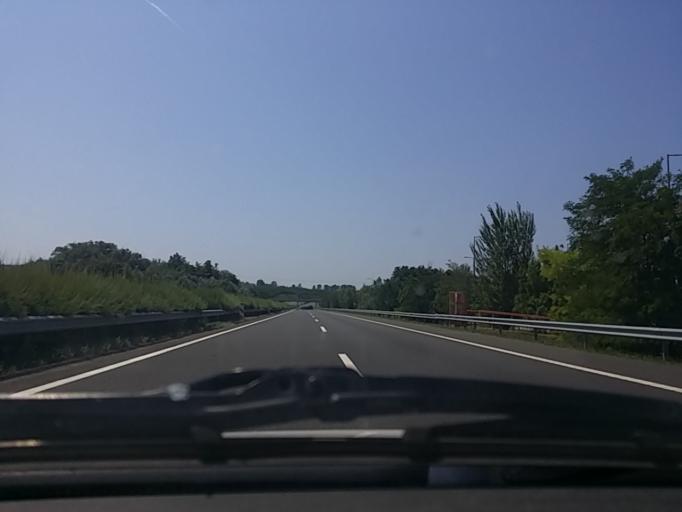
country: HU
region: Somogy
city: Balatonlelle
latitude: 46.7763
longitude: 17.7206
